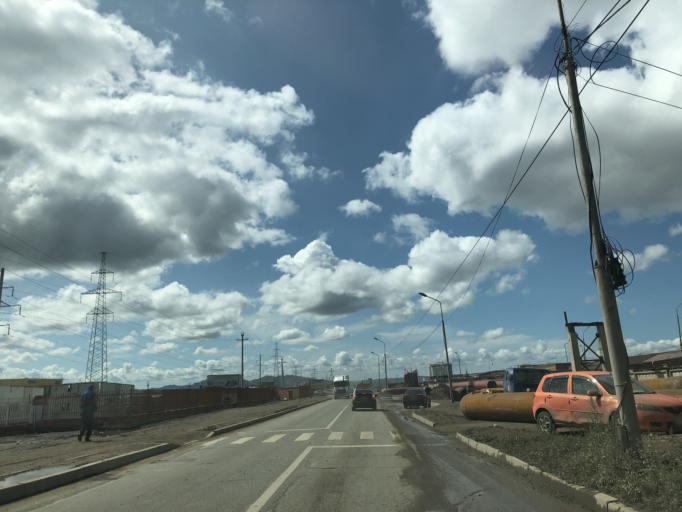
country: MN
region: Ulaanbaatar
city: Ulaanbaatar
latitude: 47.8910
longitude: 106.8002
